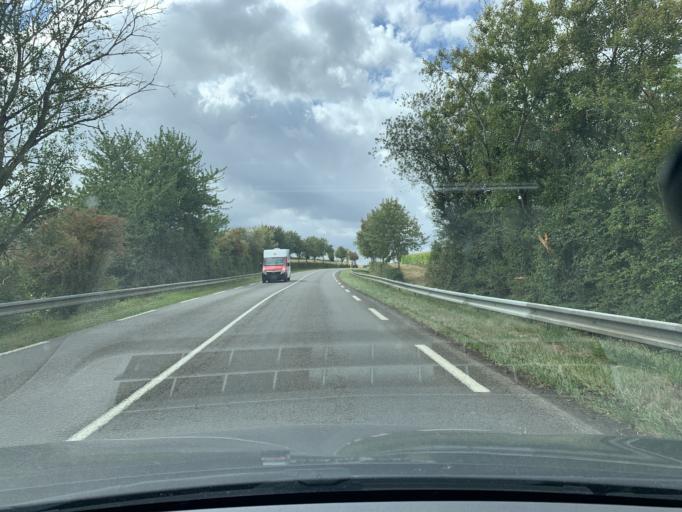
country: FR
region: Picardie
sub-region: Departement de l'Aisne
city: Hirson
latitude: 49.9090
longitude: 4.1012
